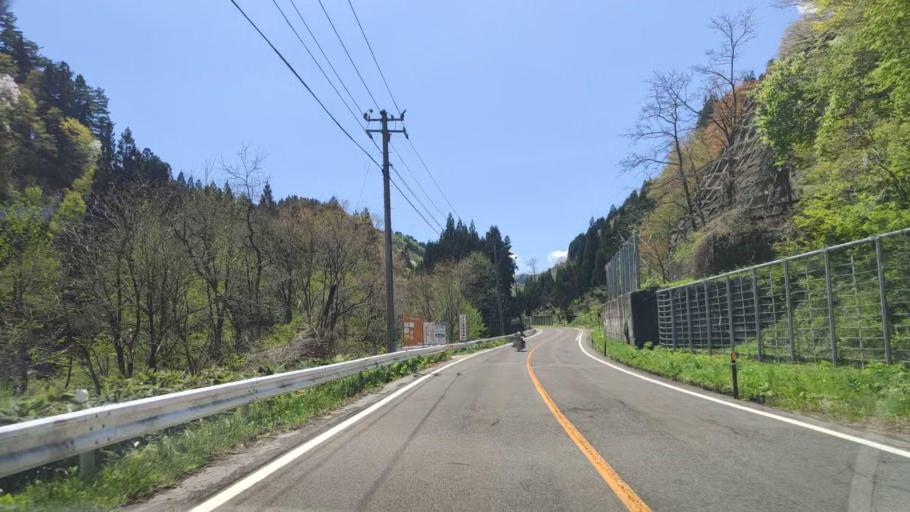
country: JP
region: Akita
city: Yuzawa
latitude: 39.0284
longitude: 140.3822
